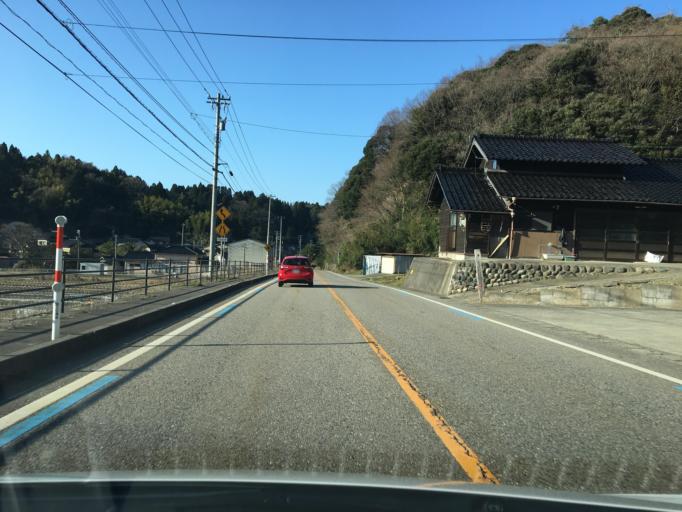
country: JP
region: Toyama
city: Himi
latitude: 36.9296
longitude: 137.0261
